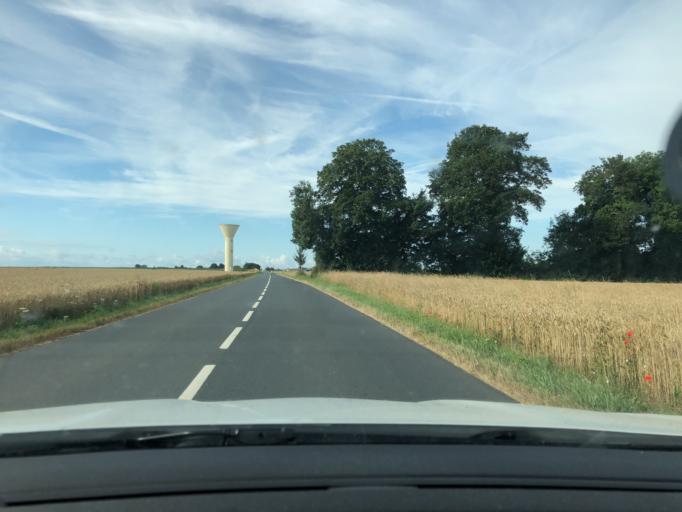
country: FR
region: Lower Normandy
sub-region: Departement du Calvados
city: Saint-Vigor-le-Grand
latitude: 49.2621
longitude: -0.6216
